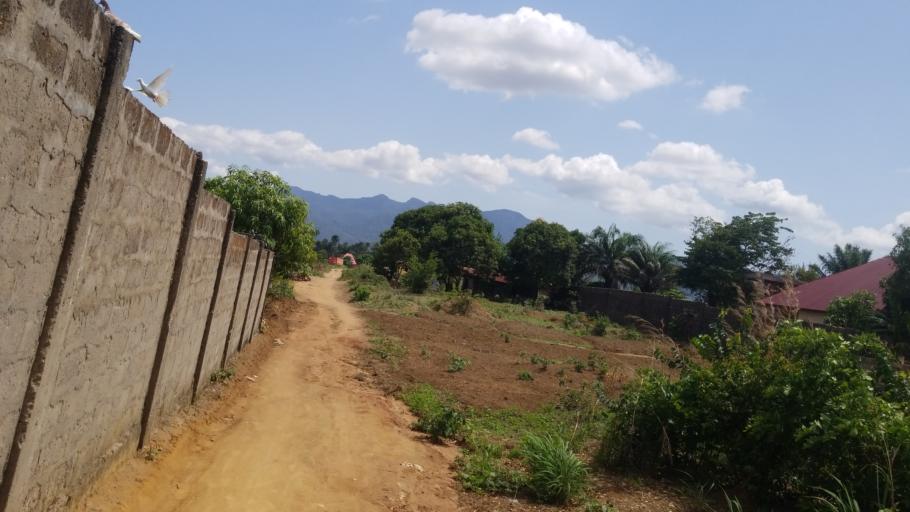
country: SL
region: Western Area
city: Waterloo
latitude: 8.3115
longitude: -13.0557
